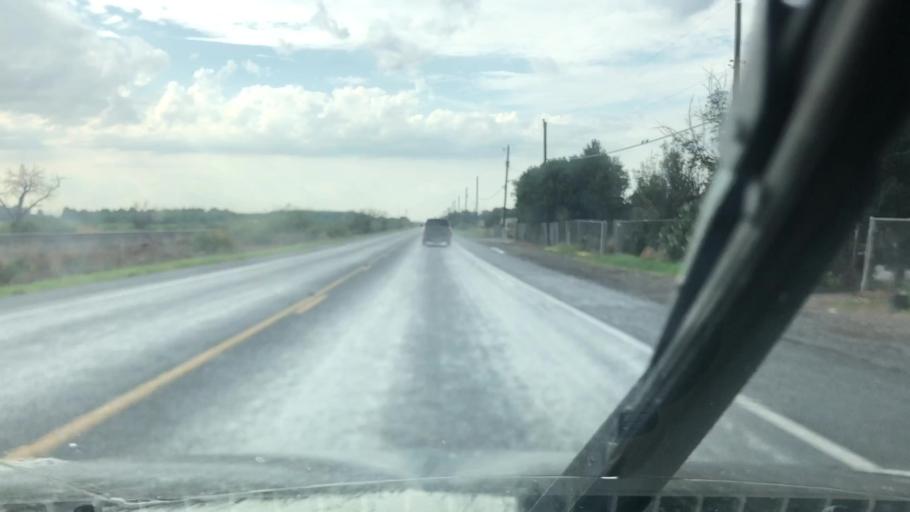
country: US
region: New Mexico
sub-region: Dona Ana County
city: Mesquite
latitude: 32.1881
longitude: -106.7114
